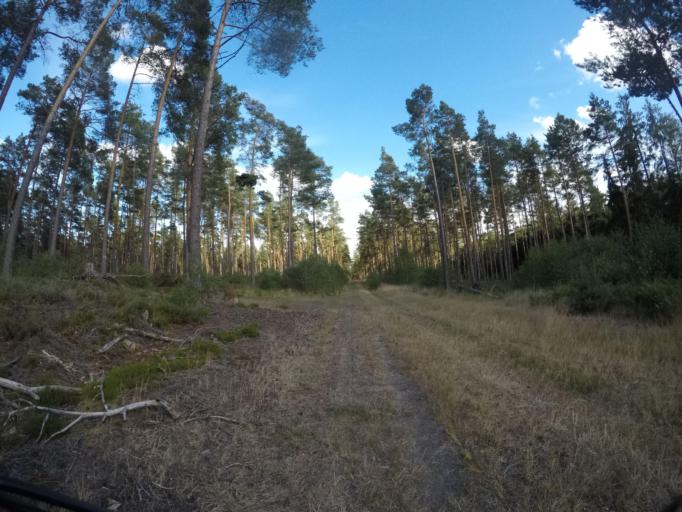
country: DE
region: Mecklenburg-Vorpommern
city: Lubtheen
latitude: 53.2499
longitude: 11.0056
